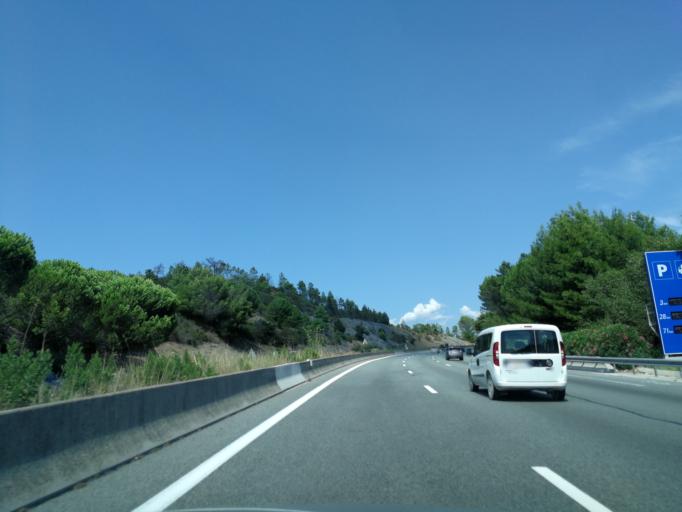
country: FR
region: Provence-Alpes-Cote d'Azur
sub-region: Departement du Var
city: Bagnols-en-Foret
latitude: 43.5204
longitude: 6.7731
